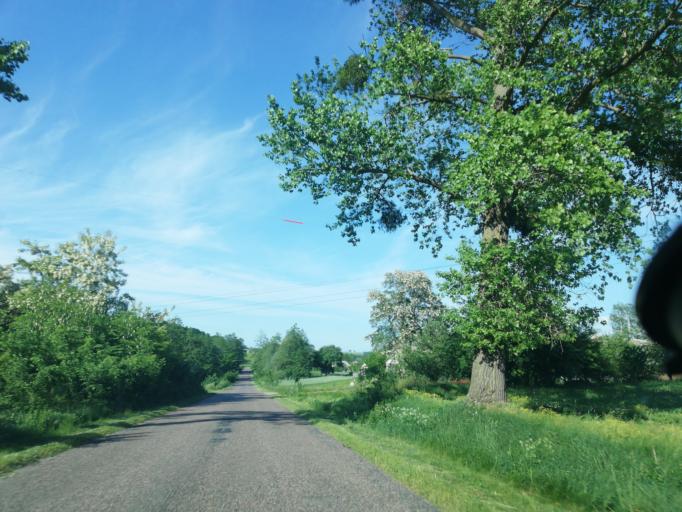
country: PL
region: Kujawsko-Pomorskie
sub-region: Powiat golubsko-dobrzynski
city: Golub-Dobrzyn
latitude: 53.0349
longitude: 19.0780
